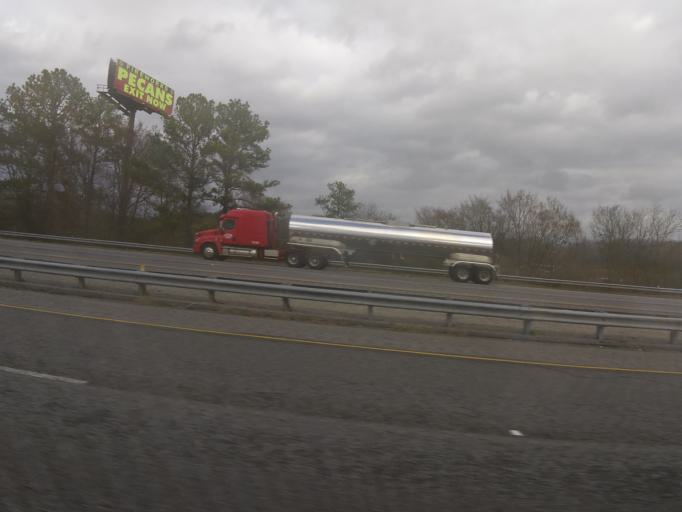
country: US
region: Georgia
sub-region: Gordon County
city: Calhoun
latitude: 34.5518
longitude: -84.9313
